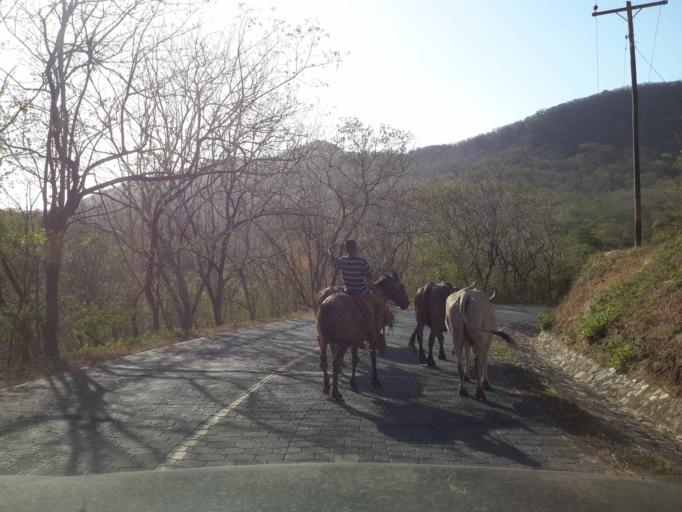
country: NI
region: Rivas
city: San Juan del Sur
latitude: 11.2273
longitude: -85.8210
